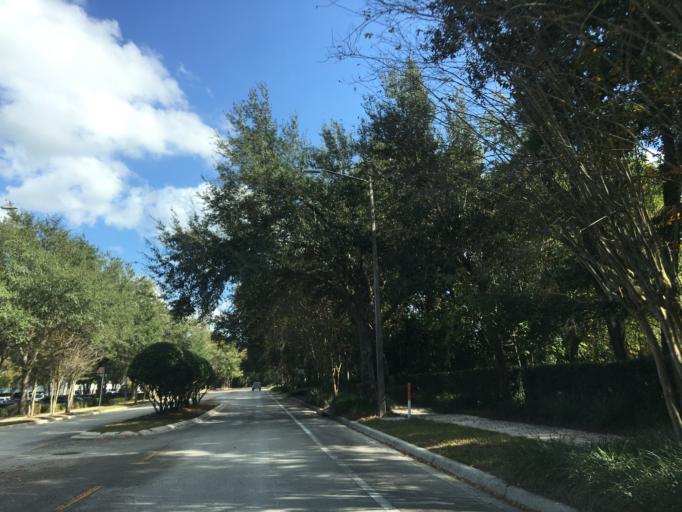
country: US
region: Florida
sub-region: Orange County
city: Eatonville
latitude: 28.6222
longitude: -81.3940
